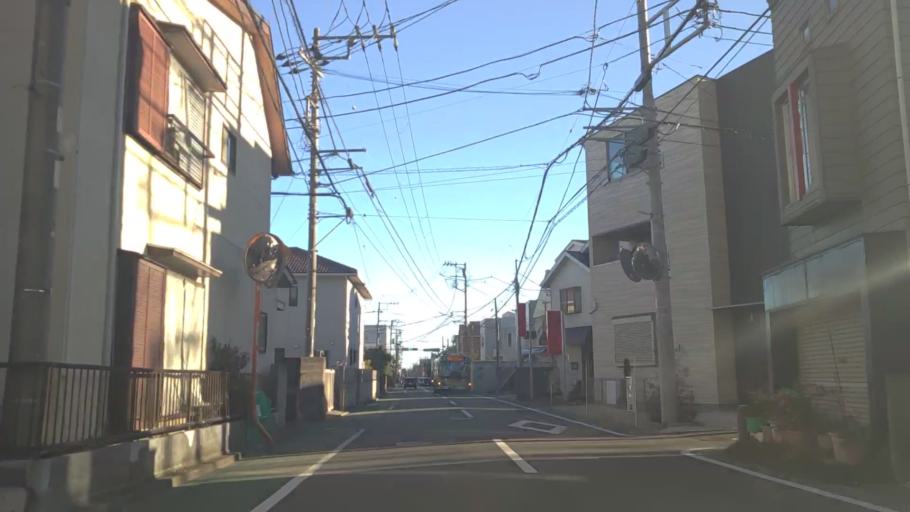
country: JP
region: Kanagawa
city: Chigasaki
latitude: 35.3285
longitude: 139.4145
